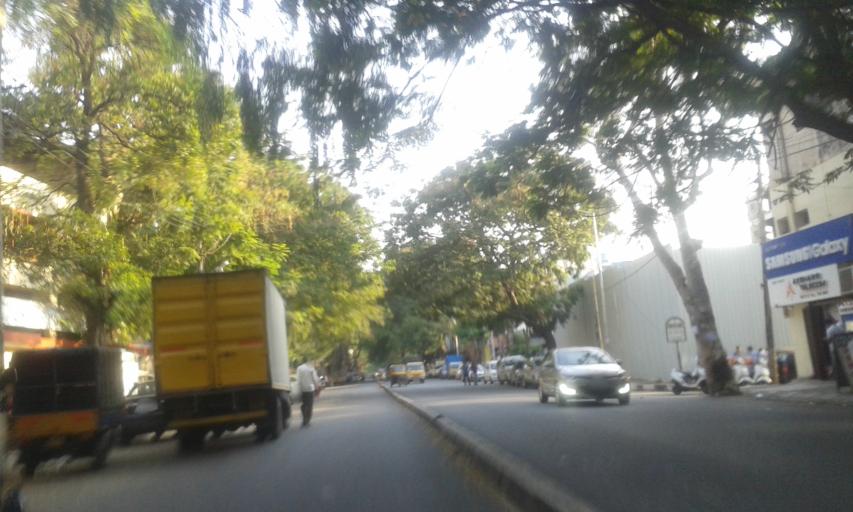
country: IN
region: Karnataka
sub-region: Bangalore Urban
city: Bangalore
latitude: 12.9527
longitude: 77.5800
